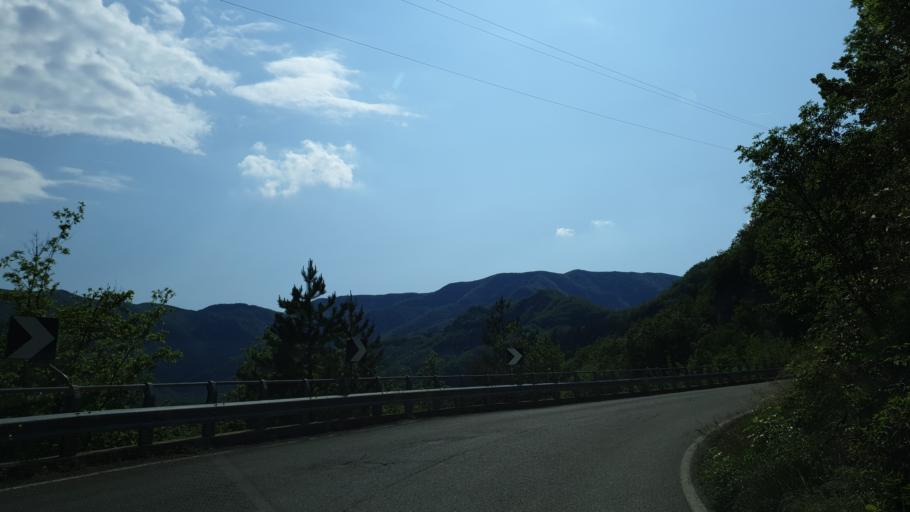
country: IT
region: Emilia-Romagna
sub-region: Forli-Cesena
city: San Piero in Bagno
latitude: 43.8154
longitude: 11.9516
